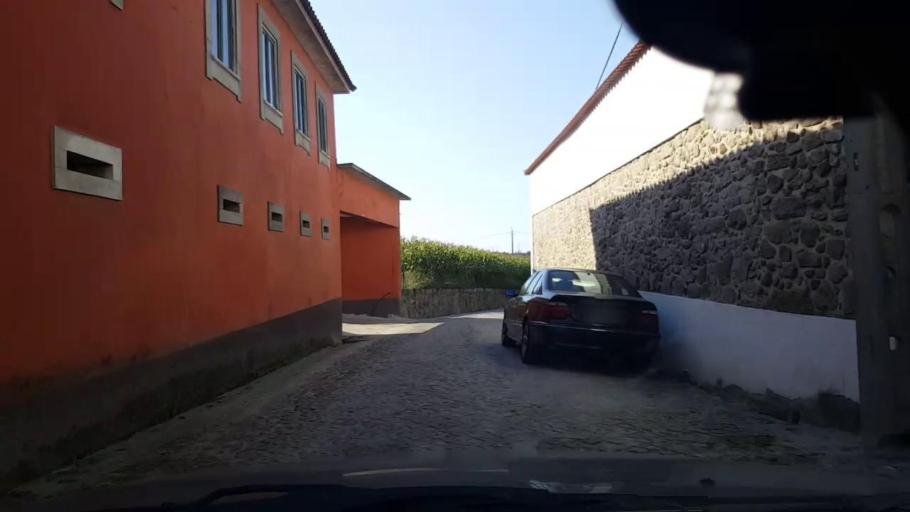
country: PT
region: Porto
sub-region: Vila do Conde
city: Arvore
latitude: 41.3573
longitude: -8.7184
